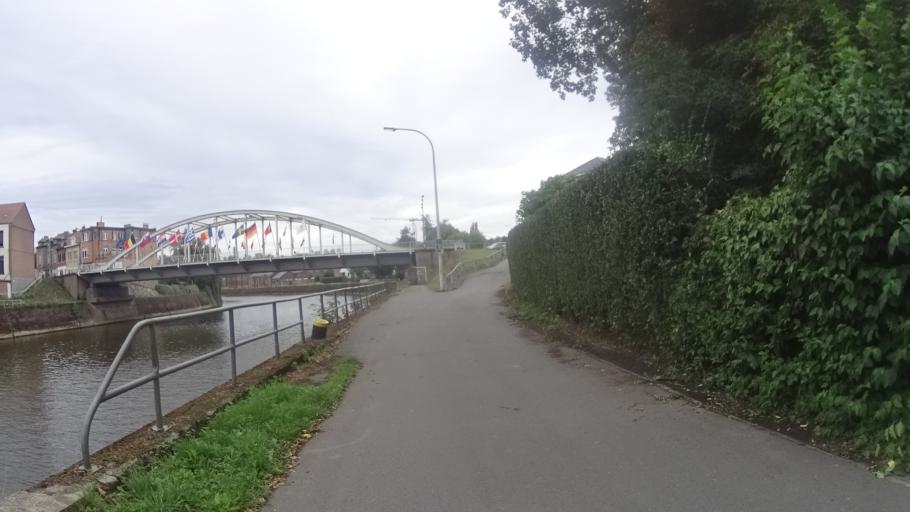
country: BE
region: Wallonia
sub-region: Province de Namur
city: La Bruyere
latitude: 50.4522
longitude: 4.6335
